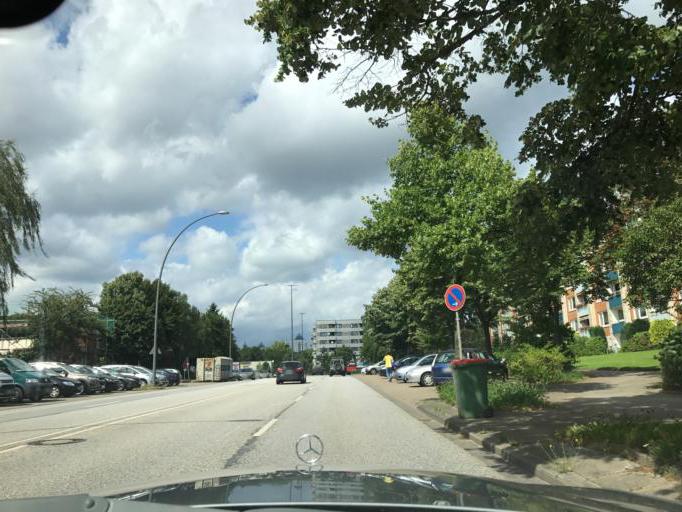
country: DE
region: Hamburg
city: Bergedorf
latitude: 53.5020
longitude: 10.2107
